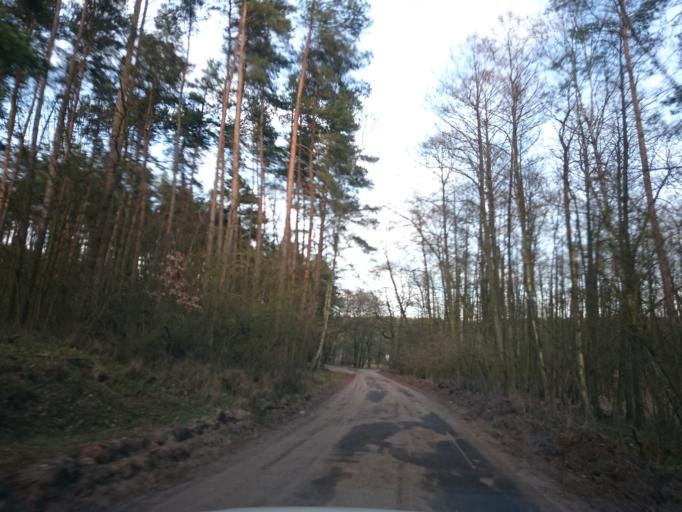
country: PL
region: Kujawsko-Pomorskie
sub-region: Powiat golubsko-dobrzynski
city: Ciechocin
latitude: 53.0712
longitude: 18.8952
